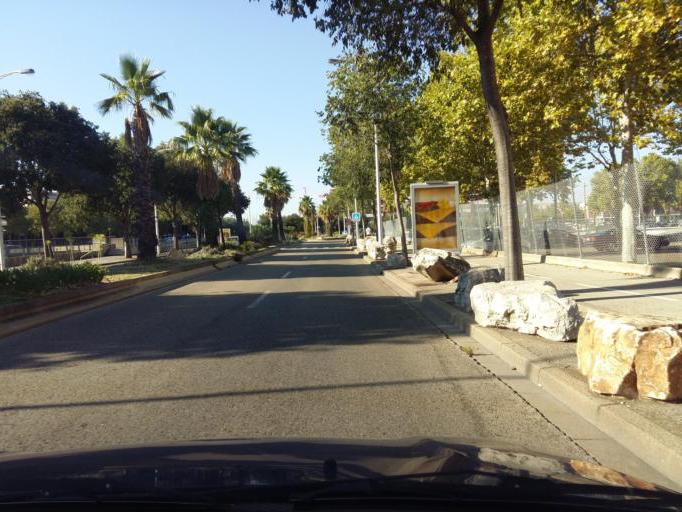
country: FR
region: Languedoc-Roussillon
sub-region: Departement du Gard
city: Nimes
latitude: 43.8157
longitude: 4.3572
